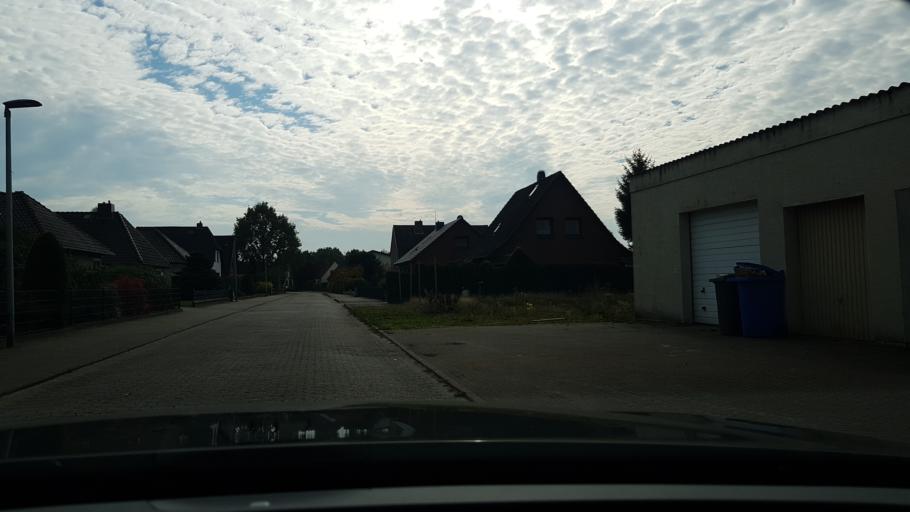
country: DE
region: Lower Saxony
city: Beverstedt
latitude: 53.4316
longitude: 8.8176
